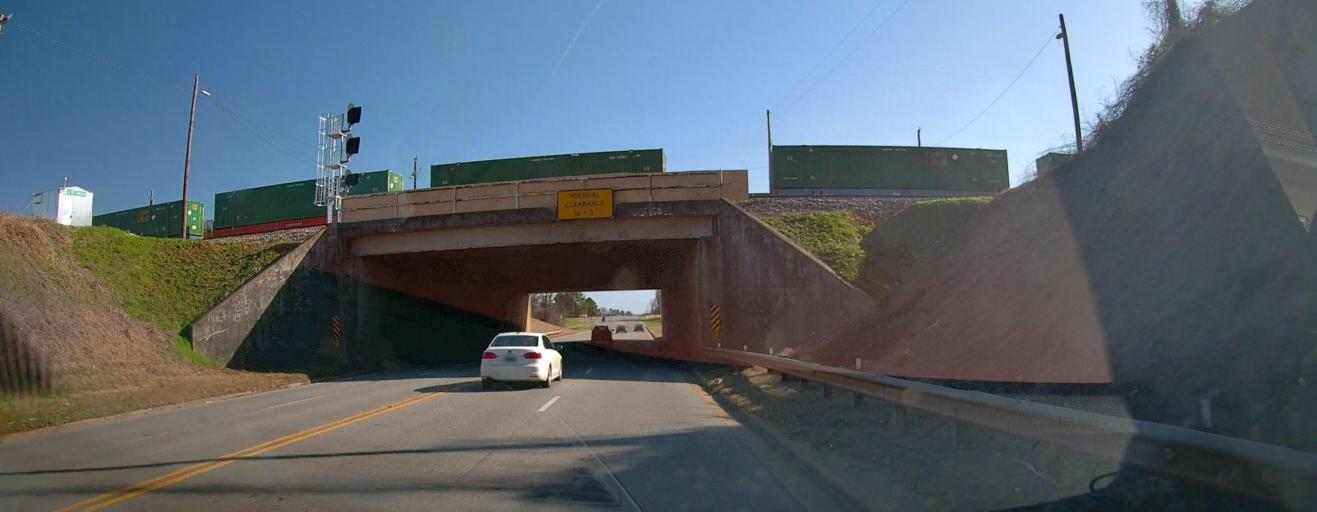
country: US
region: Alabama
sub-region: Colbert County
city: Muscle Shoals
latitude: 34.7147
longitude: -87.6350
